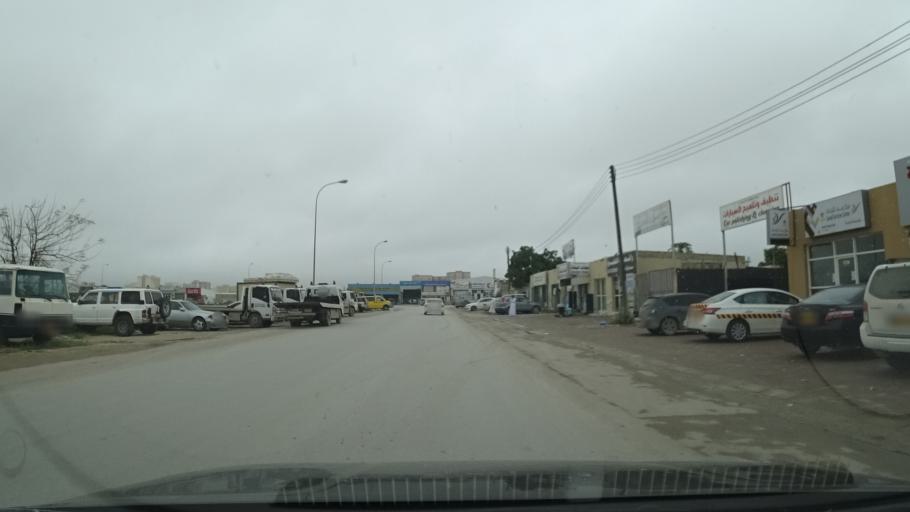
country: OM
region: Zufar
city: Salalah
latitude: 17.0176
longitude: 54.0419
